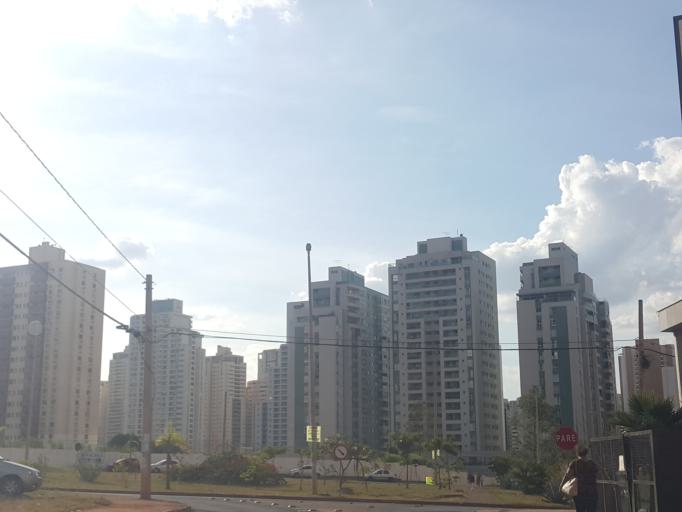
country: BR
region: Federal District
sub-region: Brasilia
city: Brasilia
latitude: -15.8438
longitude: -48.0274
